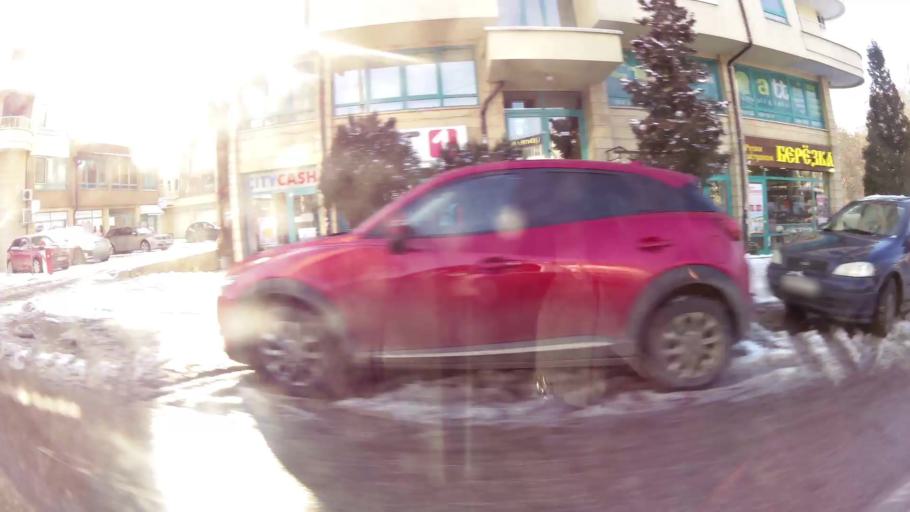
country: BG
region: Sofia-Capital
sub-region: Stolichna Obshtina
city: Sofia
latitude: 42.6646
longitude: 23.3434
